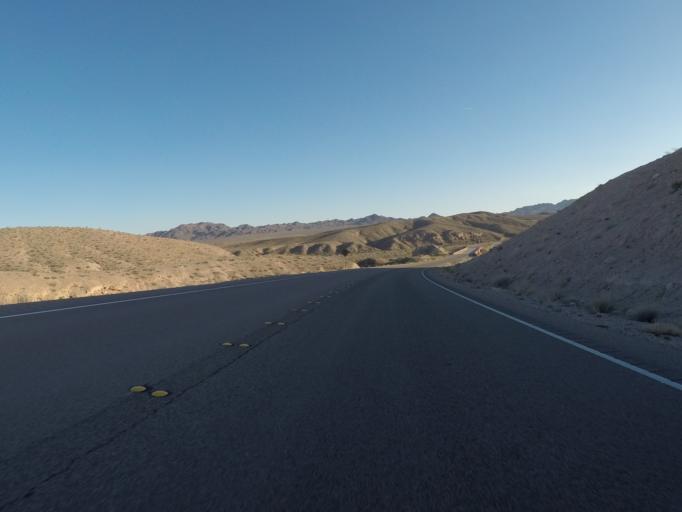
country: US
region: Nevada
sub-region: Clark County
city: Moapa Valley
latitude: 36.3114
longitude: -114.4898
